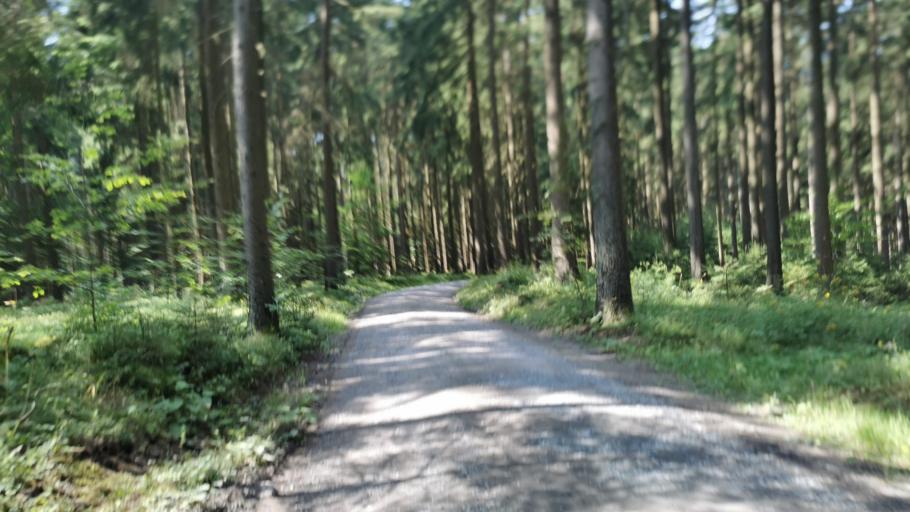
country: DE
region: Bavaria
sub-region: Upper Franconia
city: Wilhelmsthal
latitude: 50.2867
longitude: 11.3942
